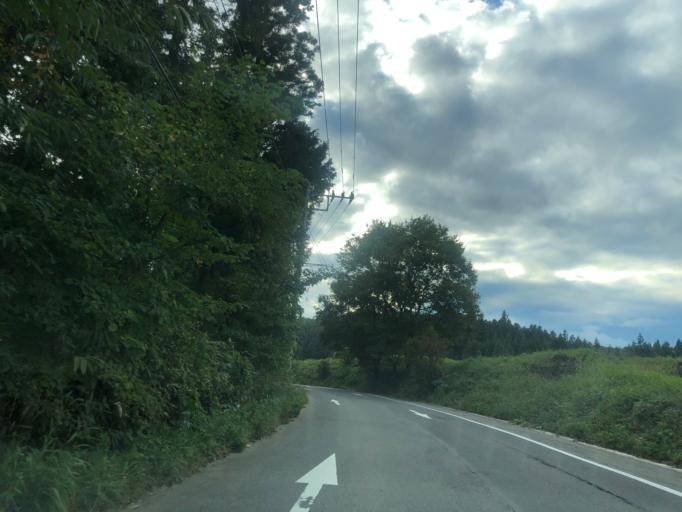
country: JP
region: Tochigi
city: Kuroiso
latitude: 36.9415
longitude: 140.1291
